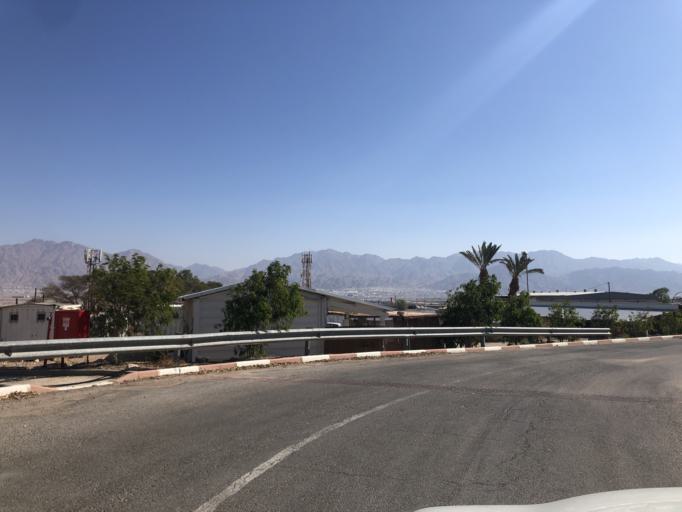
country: IL
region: Southern District
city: Eilat
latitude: 29.5825
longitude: 34.9640
